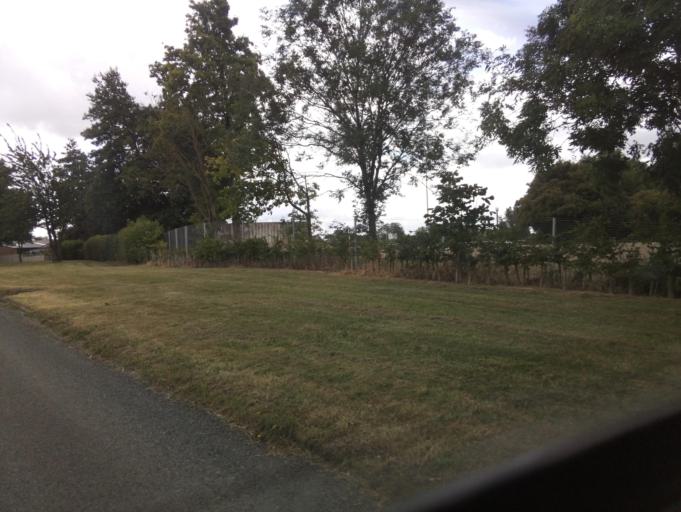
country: GB
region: England
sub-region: Wiltshire
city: Royal Wootton Bassett
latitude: 51.5565
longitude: -1.9010
